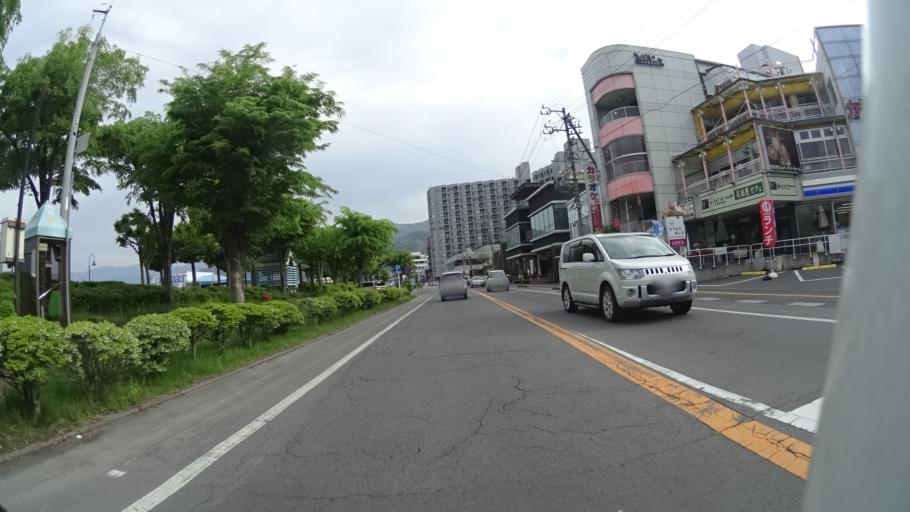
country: JP
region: Nagano
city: Suwa
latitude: 36.0499
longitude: 138.1128
